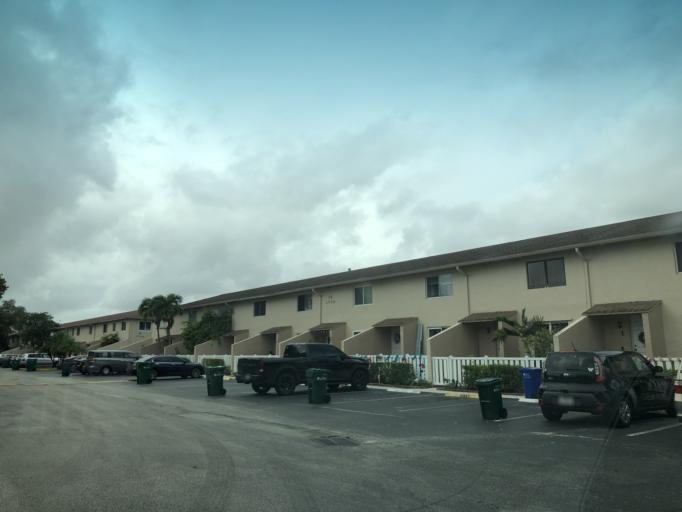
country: US
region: Florida
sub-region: Broward County
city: Margate
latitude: 26.2499
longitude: -80.2307
